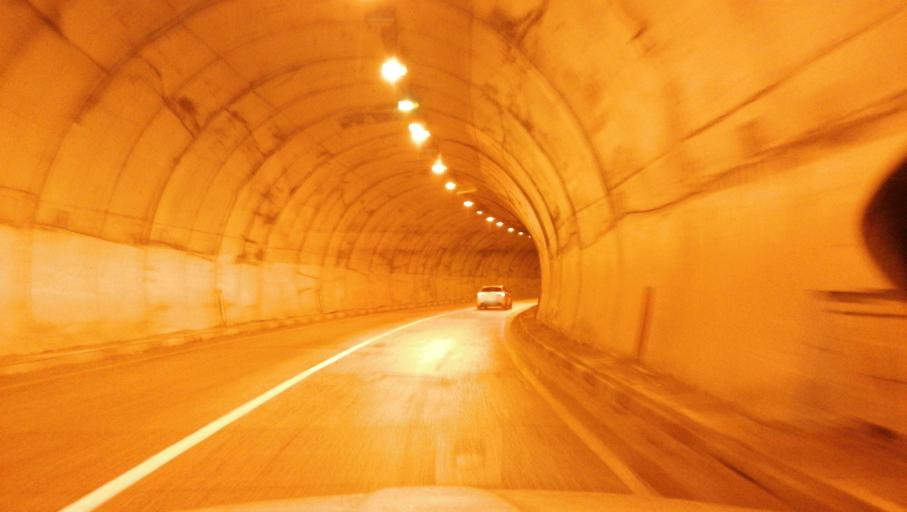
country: BA
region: Republika Srpska
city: Cajnice
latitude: 43.6809
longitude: 19.1490
